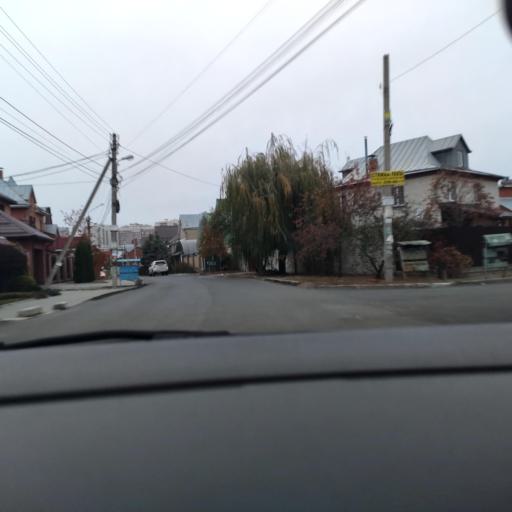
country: RU
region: Voronezj
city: Voronezh
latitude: 51.7048
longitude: 39.2043
